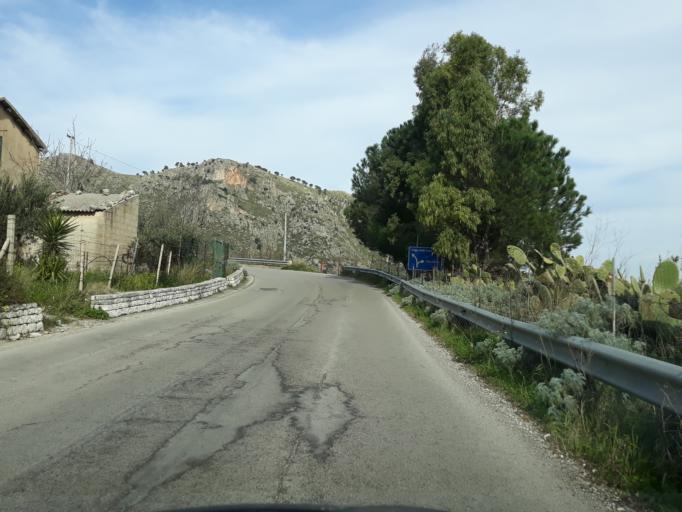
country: IT
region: Sicily
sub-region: Palermo
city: Altofonte
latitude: 38.0422
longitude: 13.3099
